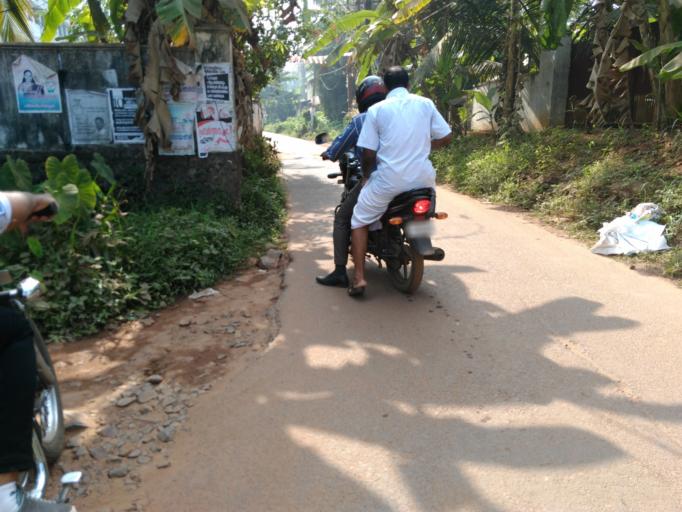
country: IN
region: Kerala
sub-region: Kozhikode
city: Kozhikode
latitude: 11.2766
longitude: 75.8279
